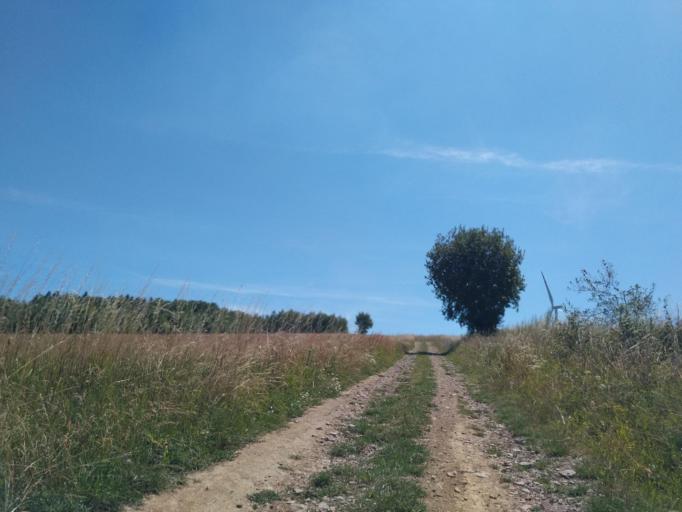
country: PL
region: Subcarpathian Voivodeship
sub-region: Powiat sanocki
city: Bukowsko
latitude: 49.5151
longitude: 22.0469
